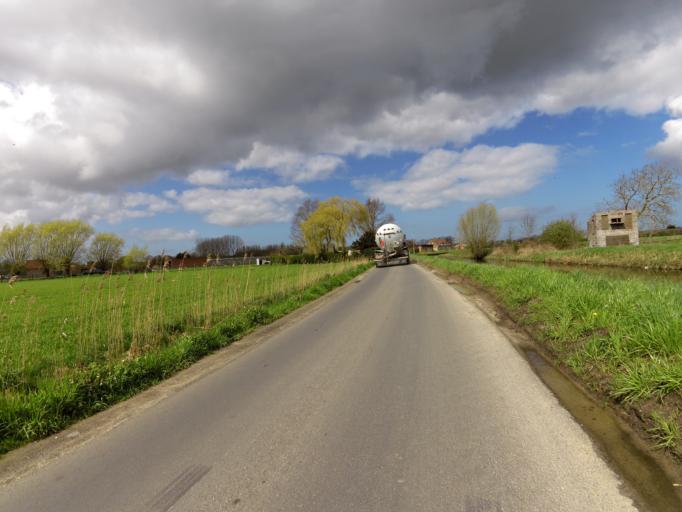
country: BE
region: Flanders
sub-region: Provincie West-Vlaanderen
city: Oudenburg
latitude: 51.1544
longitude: 2.9997
